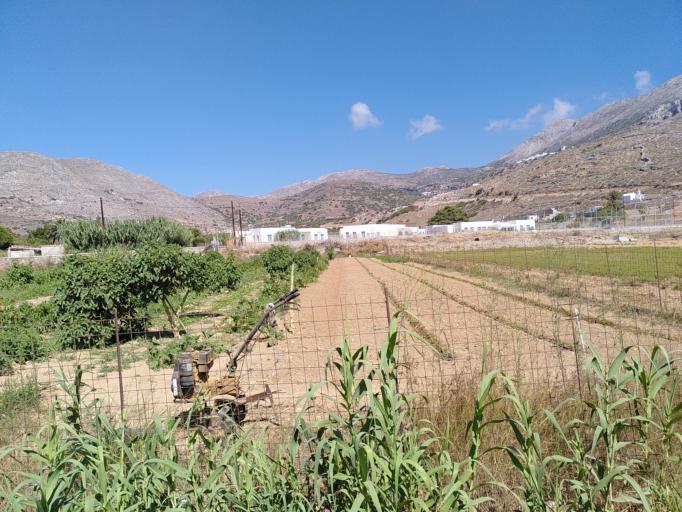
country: GR
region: South Aegean
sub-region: Nomos Kykladon
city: Amorgos
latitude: 36.9049
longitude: 25.9795
